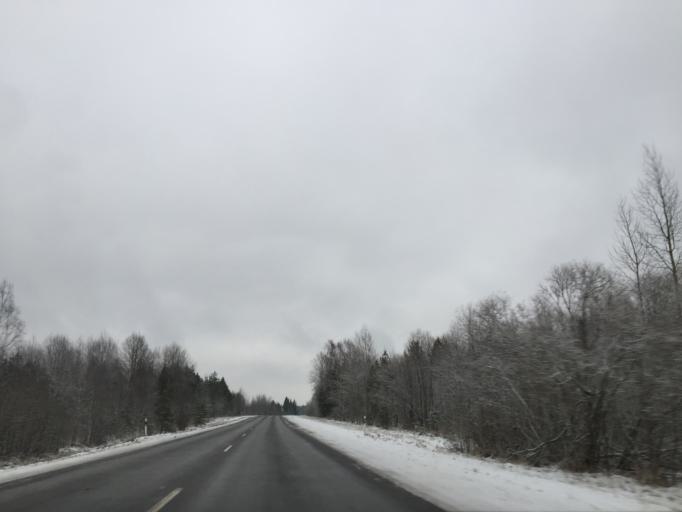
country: EE
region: Laeaene
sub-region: Lihula vald
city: Lihula
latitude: 58.6237
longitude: 23.8959
